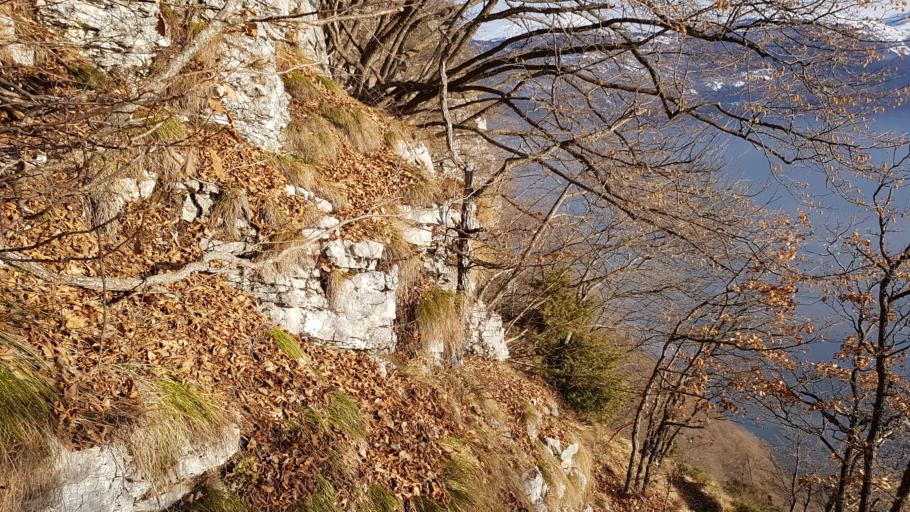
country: IT
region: Trentino-Alto Adige
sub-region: Provincia di Trento
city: Padergnone
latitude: 46.0674
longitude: 10.9550
